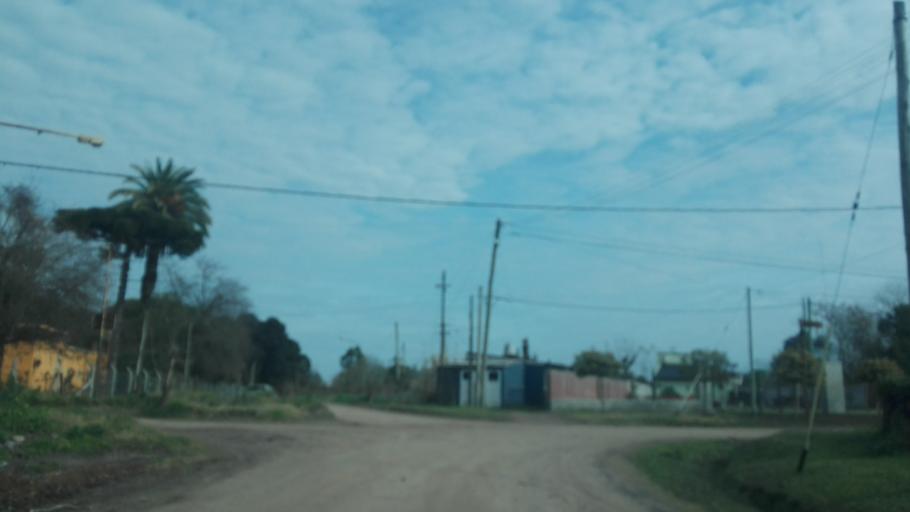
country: AR
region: Buenos Aires
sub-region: Partido de Chascomus
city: Chascomus
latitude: -35.5819
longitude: -57.9872
